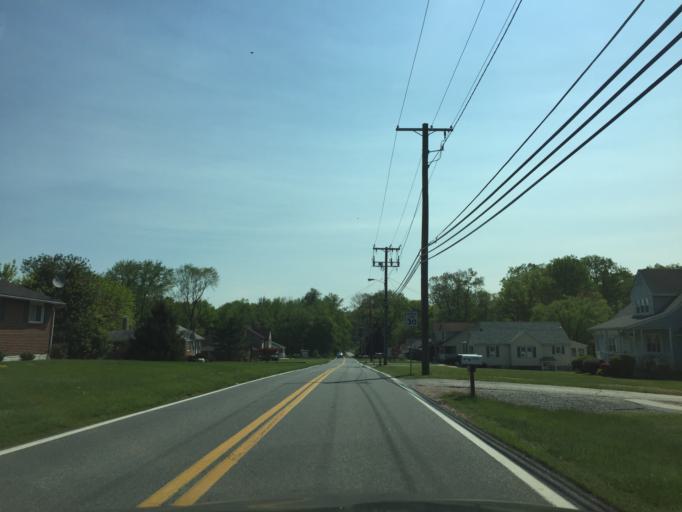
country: US
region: Maryland
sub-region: Baltimore County
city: White Marsh
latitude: 39.3661
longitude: -76.4189
